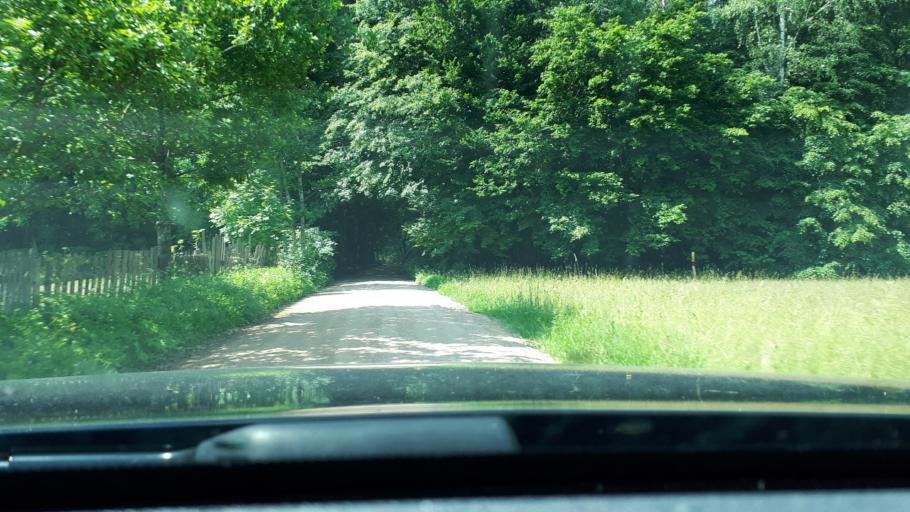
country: PL
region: Podlasie
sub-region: Powiat bialostocki
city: Suprasl
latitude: 53.2407
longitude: 23.3471
